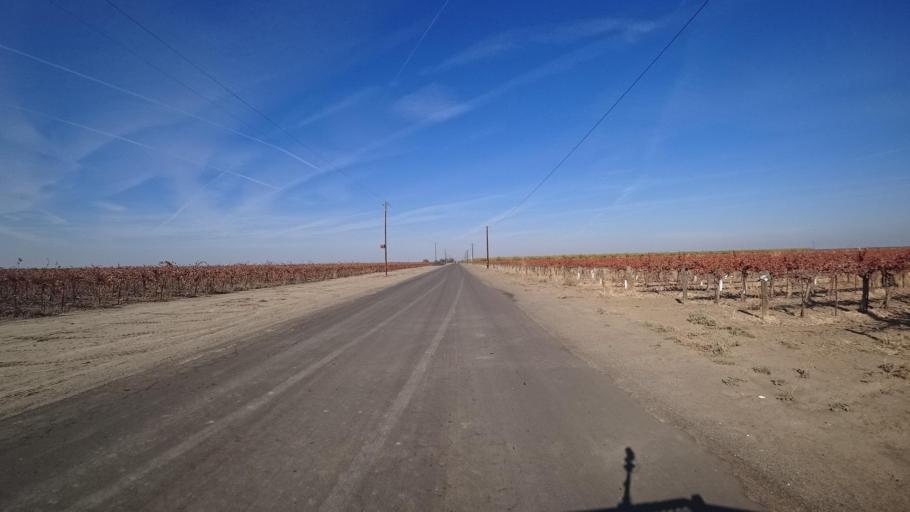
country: US
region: California
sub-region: Kern County
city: Wasco
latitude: 35.6970
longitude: -119.3839
